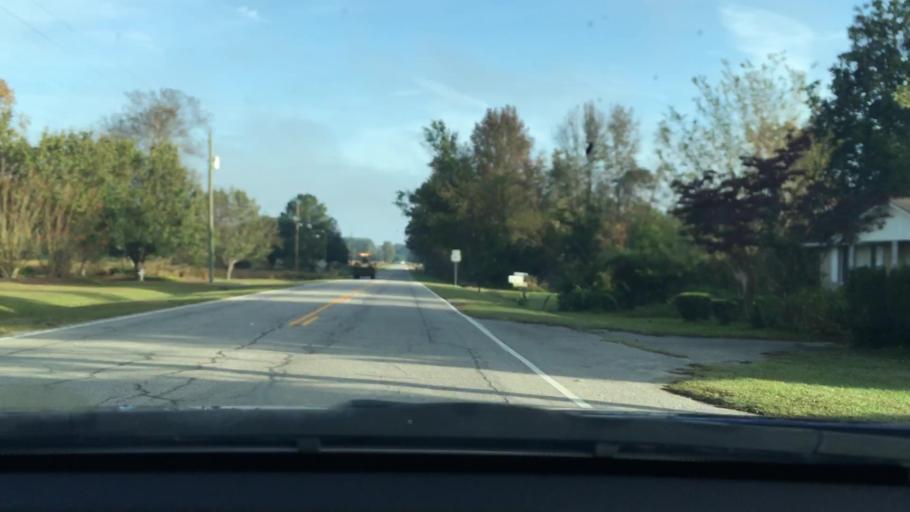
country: US
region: South Carolina
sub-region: Sumter County
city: East Sumter
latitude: 33.9983
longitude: -80.2890
